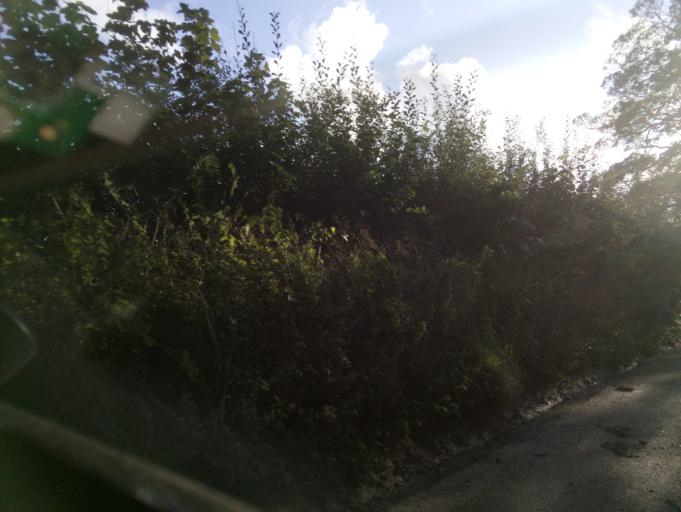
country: GB
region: England
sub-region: Devon
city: Totnes
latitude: 50.3457
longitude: -3.6671
